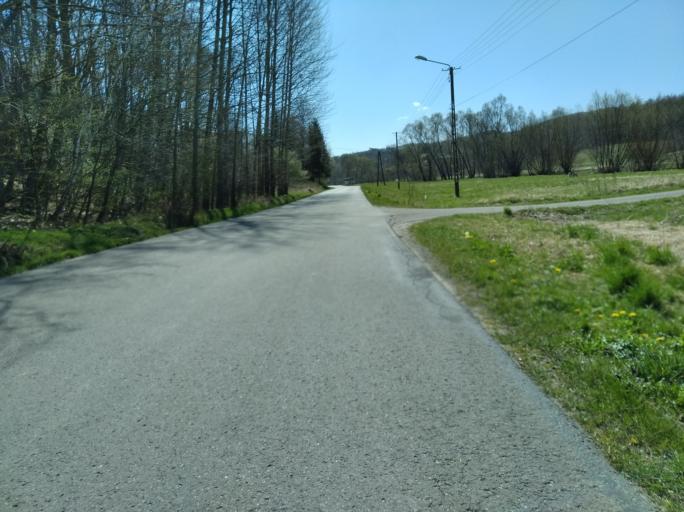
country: PL
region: Subcarpathian Voivodeship
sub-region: Powiat brzozowski
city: Jablonka
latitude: 49.7394
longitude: 22.1343
